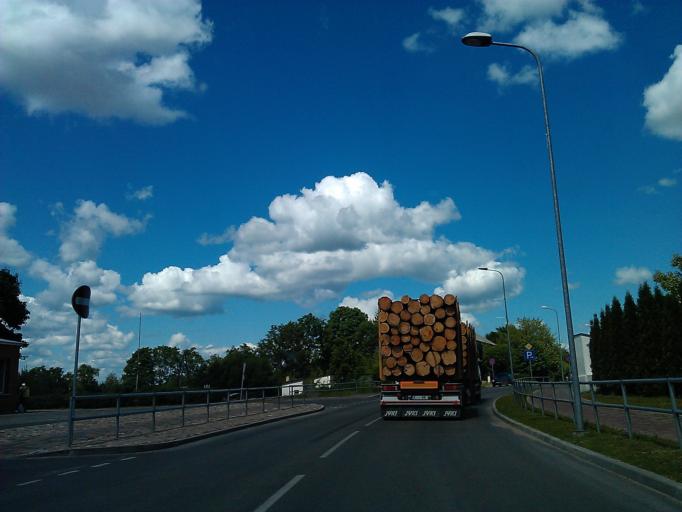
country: LV
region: Vilanu
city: Vilani
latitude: 56.5524
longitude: 26.9220
